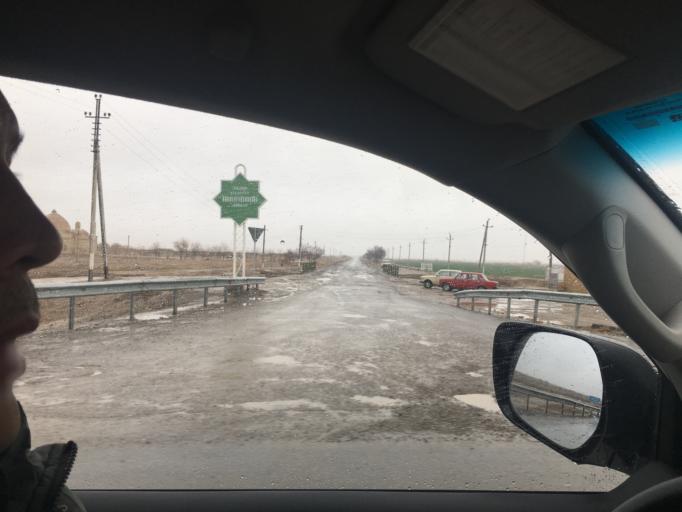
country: TM
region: Mary
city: Bayramaly
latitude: 37.4095
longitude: 62.1687
